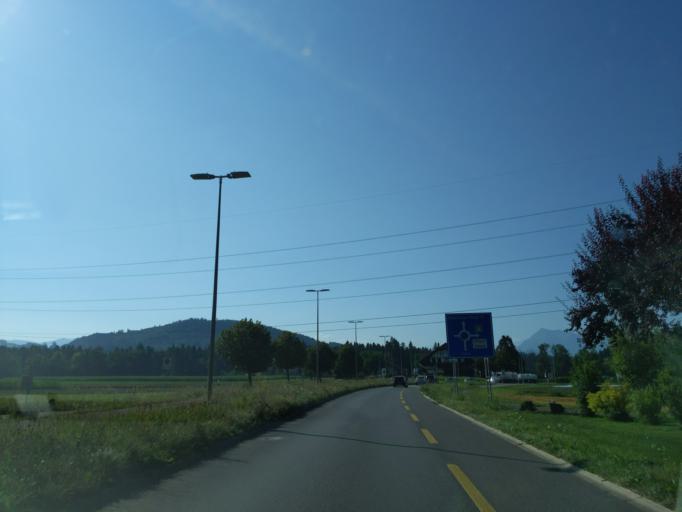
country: CH
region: Bern
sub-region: Thun District
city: Heimberg
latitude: 46.8142
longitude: 7.5914
